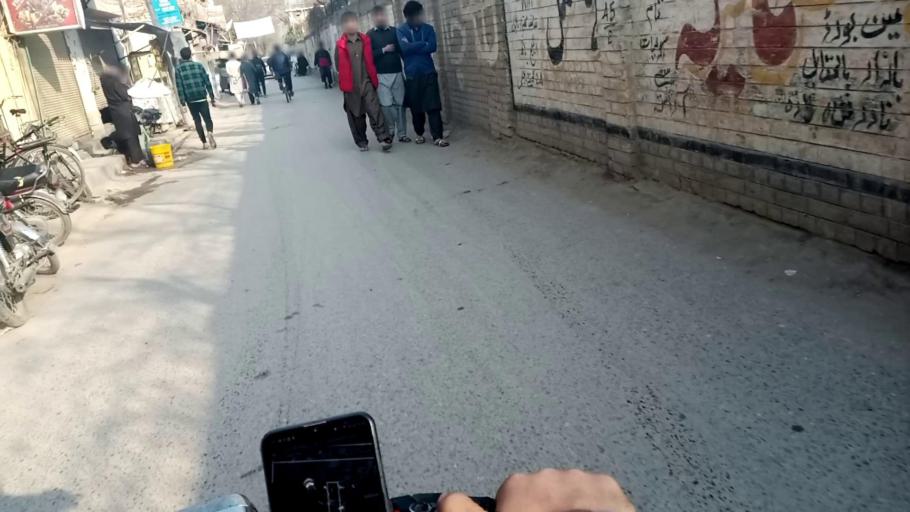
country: PK
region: Khyber Pakhtunkhwa
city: Peshawar
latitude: 34.0056
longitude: 71.4746
